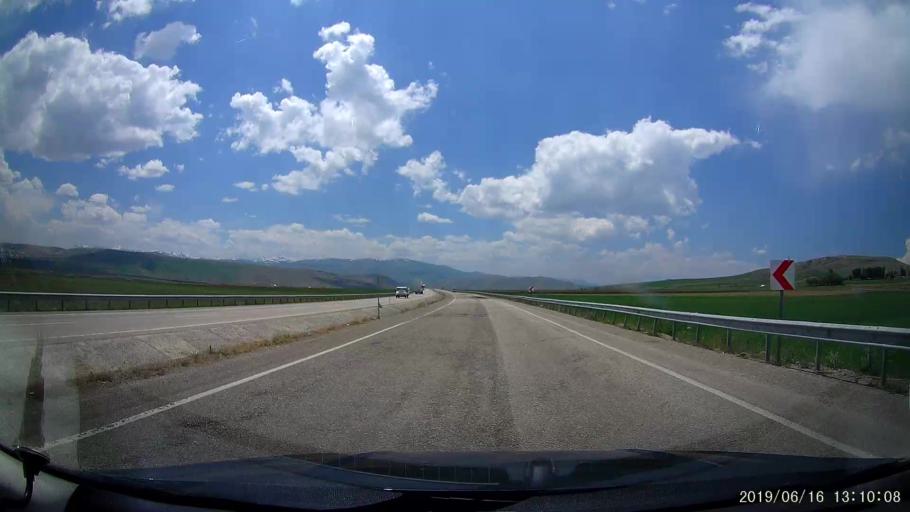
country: TR
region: Agri
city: Diyadin
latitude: 39.5973
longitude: 43.6392
